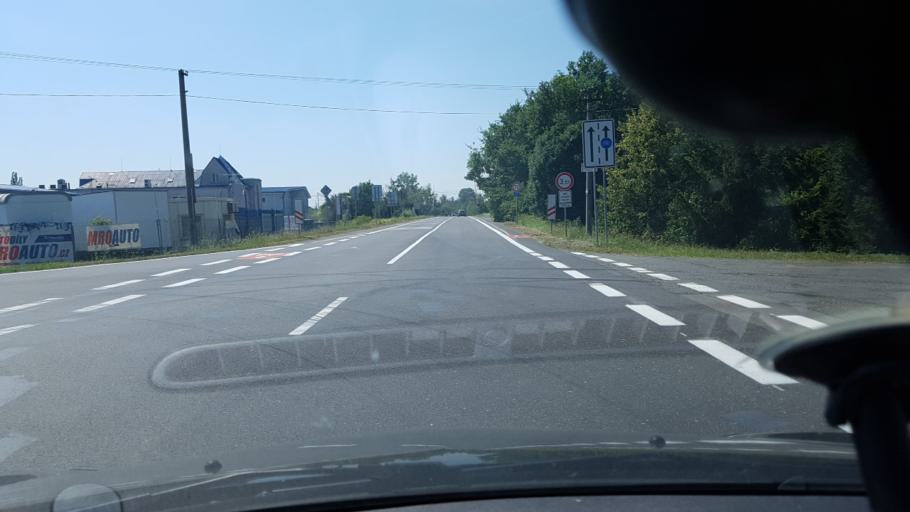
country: CZ
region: Moravskoslezsky
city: Stary Bohumin
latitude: 49.9075
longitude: 18.3371
